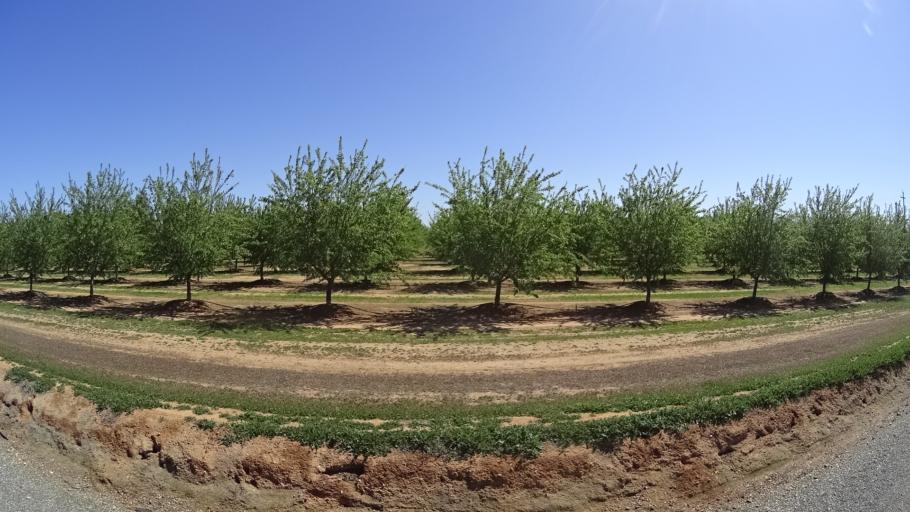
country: US
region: California
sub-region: Glenn County
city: Orland
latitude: 39.6688
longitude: -122.2531
